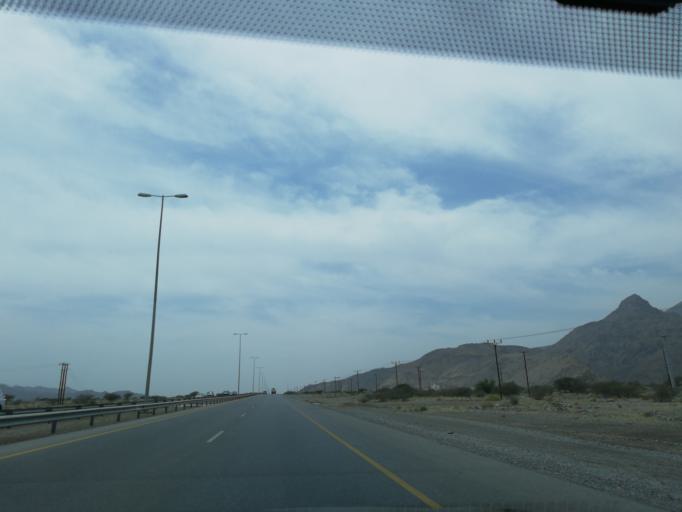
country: OM
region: Muhafazat ad Dakhiliyah
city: Izki
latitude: 23.0797
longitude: 57.8192
